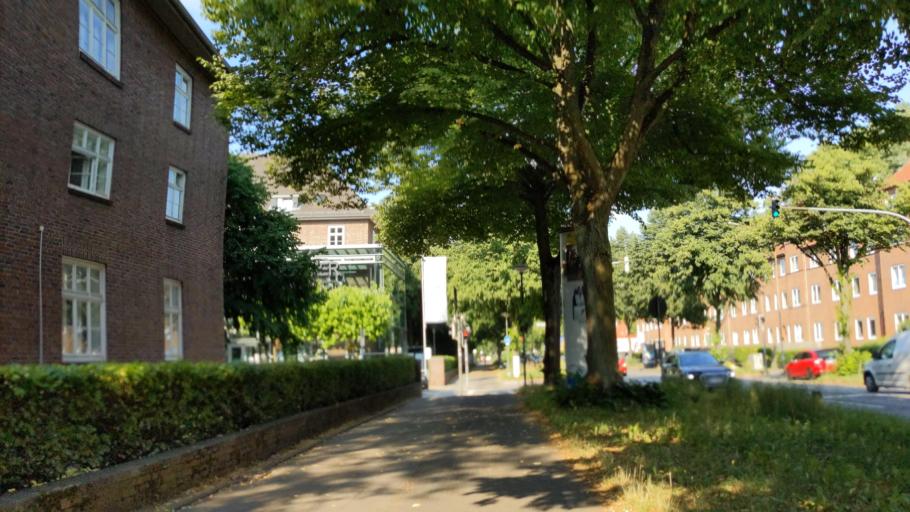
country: DE
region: Schleswig-Holstein
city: Luebeck
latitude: 53.8639
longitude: 10.7159
